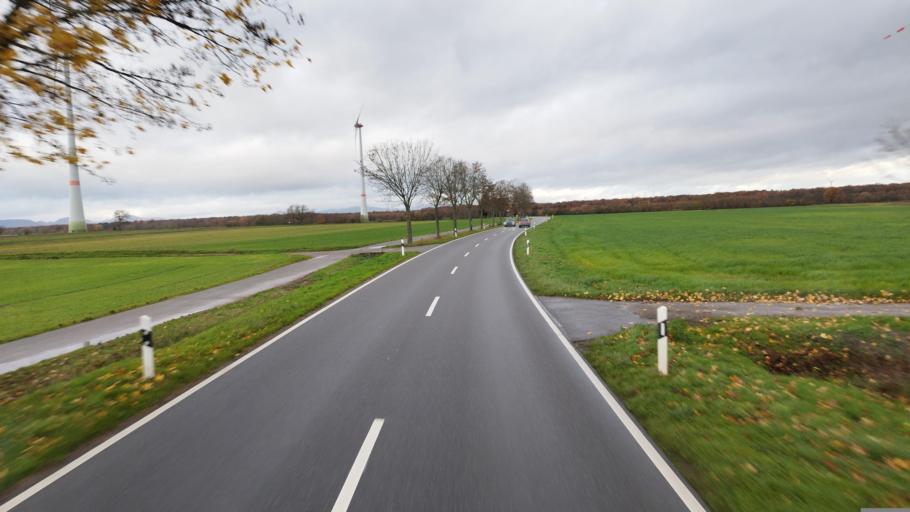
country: DE
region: Rheinland-Pfalz
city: Hatzenbuhl
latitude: 49.1188
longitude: 8.2379
